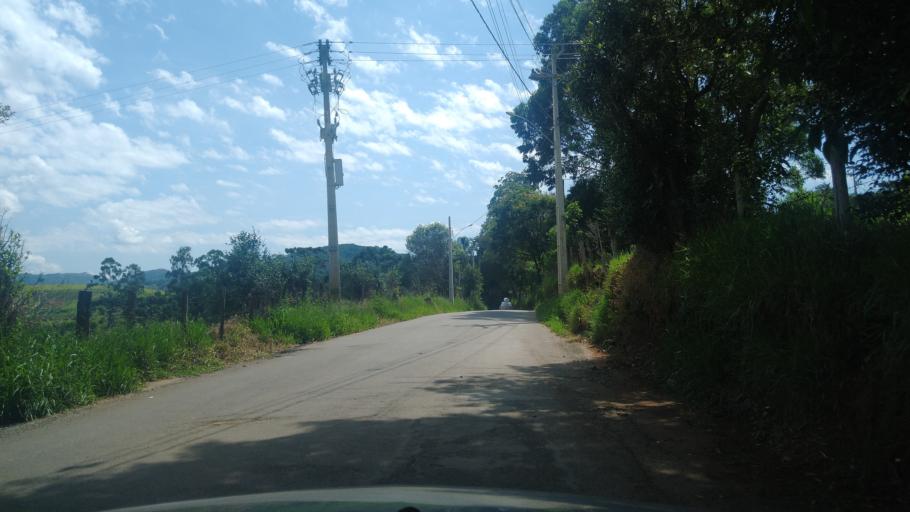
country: BR
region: Minas Gerais
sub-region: Extrema
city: Extrema
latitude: -22.7999
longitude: -46.2958
